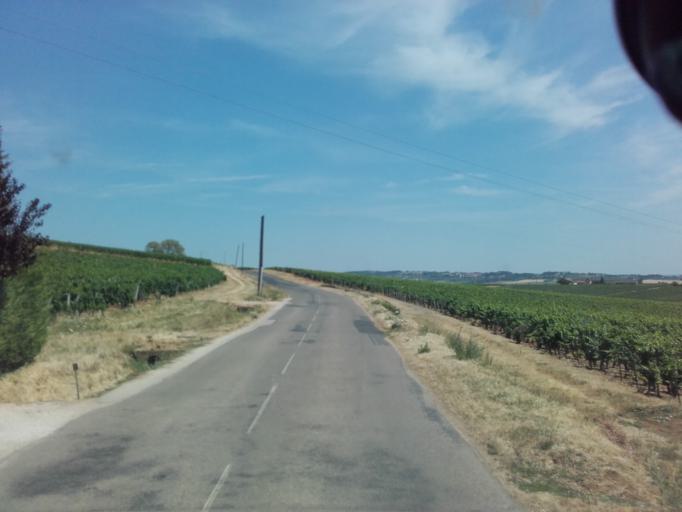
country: FR
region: Bourgogne
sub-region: Departement de Saone-et-Loire
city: Prisse
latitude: 46.2847
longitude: 4.7412
